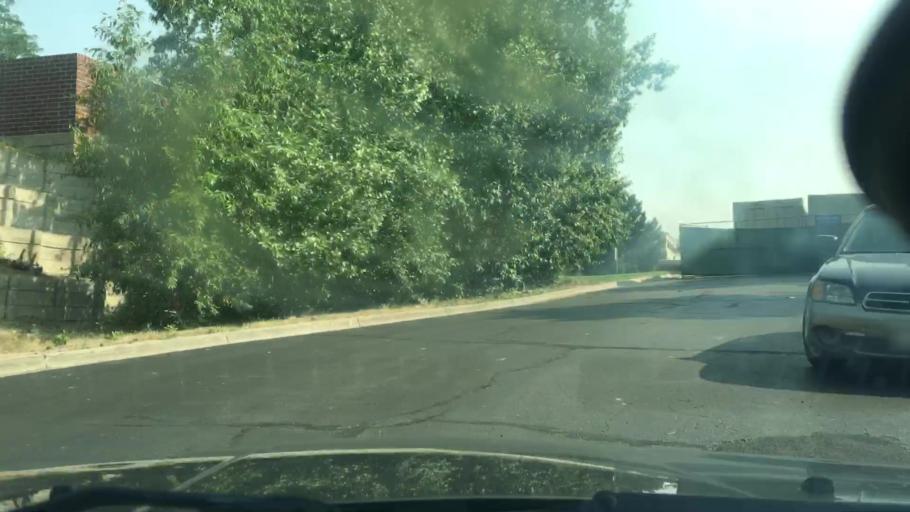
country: US
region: Colorado
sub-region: Douglas County
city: Acres Green
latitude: 39.5666
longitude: -104.9079
